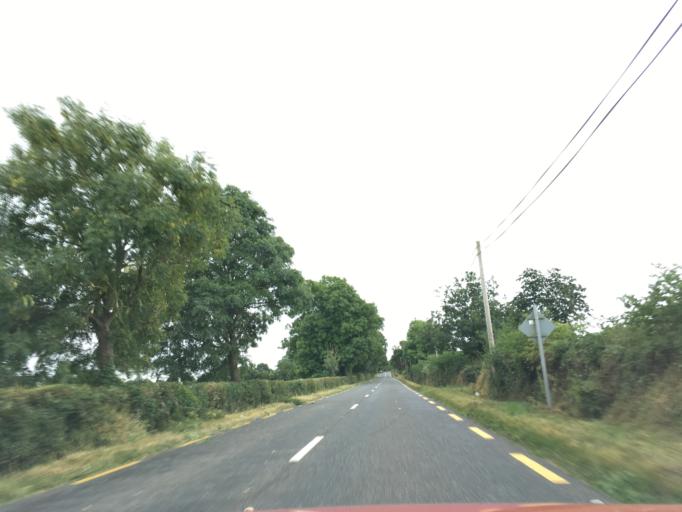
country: IE
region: Munster
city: Fethard
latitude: 52.4347
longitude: -7.7889
